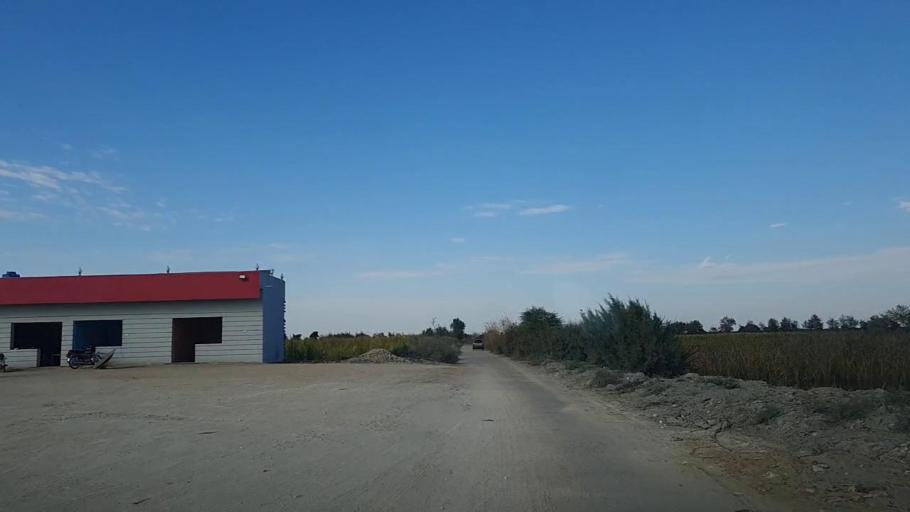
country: PK
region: Sindh
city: Khadro
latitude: 26.2792
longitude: 68.8200
